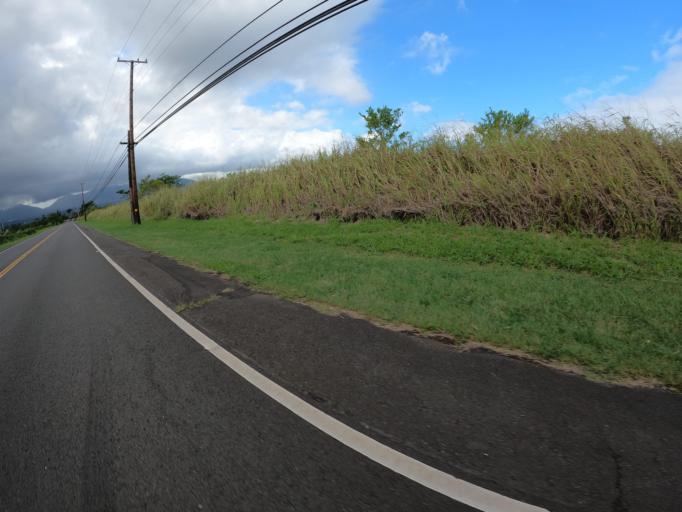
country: US
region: Hawaii
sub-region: Honolulu County
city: Whitmore Village
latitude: 21.5125
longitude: -158.0139
